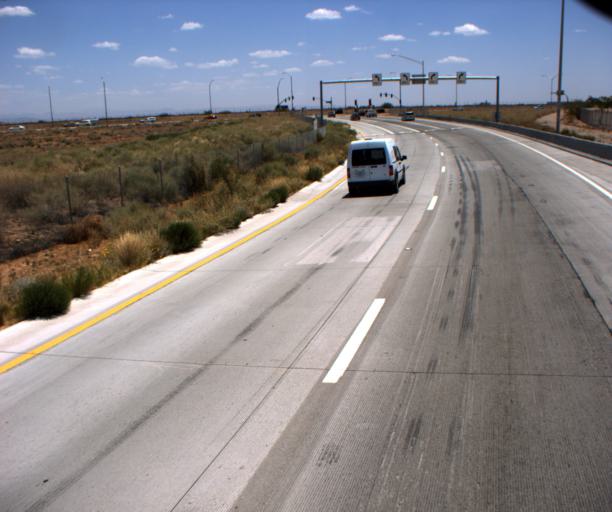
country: US
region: Arizona
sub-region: Maricopa County
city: Queen Creek
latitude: 33.3170
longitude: -111.6377
